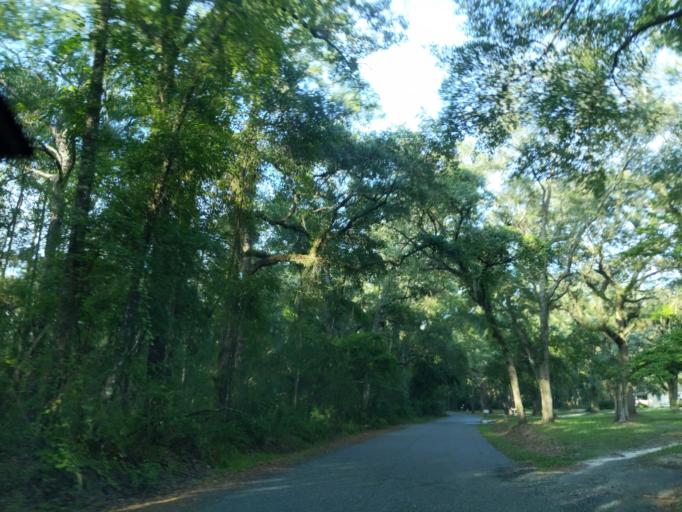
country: US
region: Florida
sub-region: Leon County
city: Woodville
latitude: 30.3488
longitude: -84.3659
